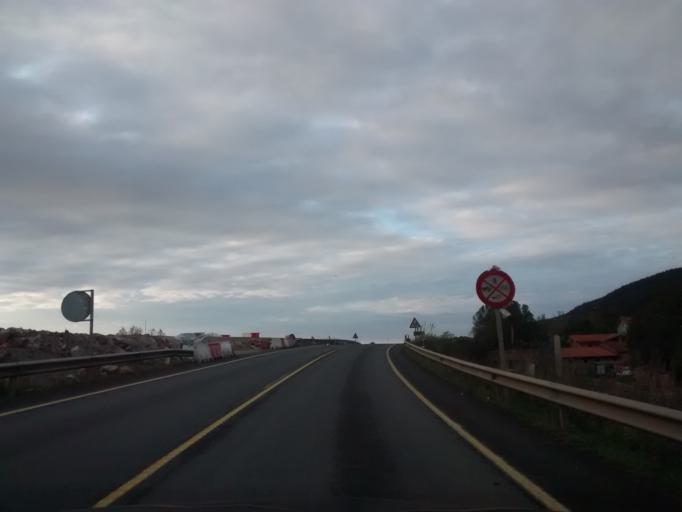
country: ES
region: Cantabria
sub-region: Provincia de Cantabria
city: Puente Viesgo
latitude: 43.3124
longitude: -3.9448
